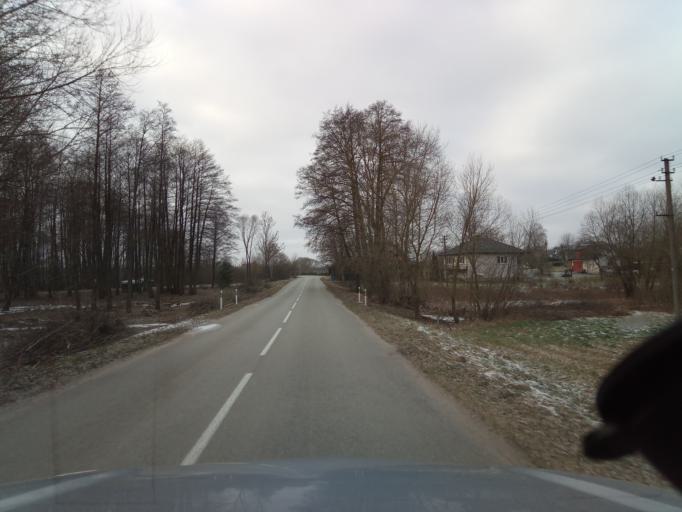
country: LT
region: Alytaus apskritis
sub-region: Alytaus rajonas
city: Daugai
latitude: 54.3572
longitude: 24.3365
